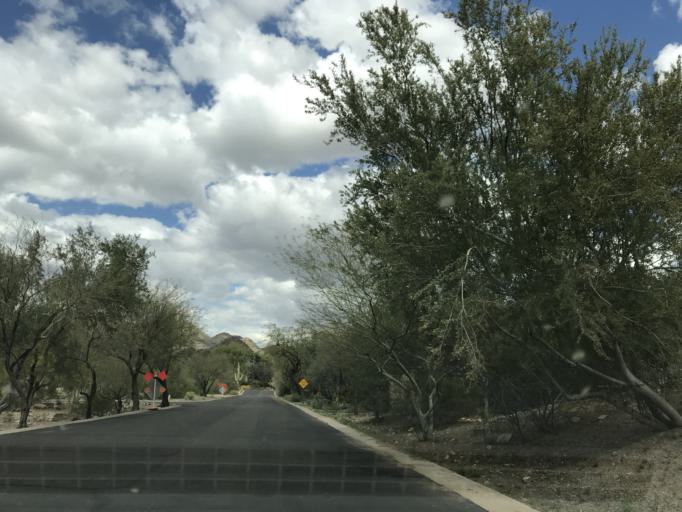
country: US
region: Arizona
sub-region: Maricopa County
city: Paradise Valley
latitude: 33.5221
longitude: -112.0066
